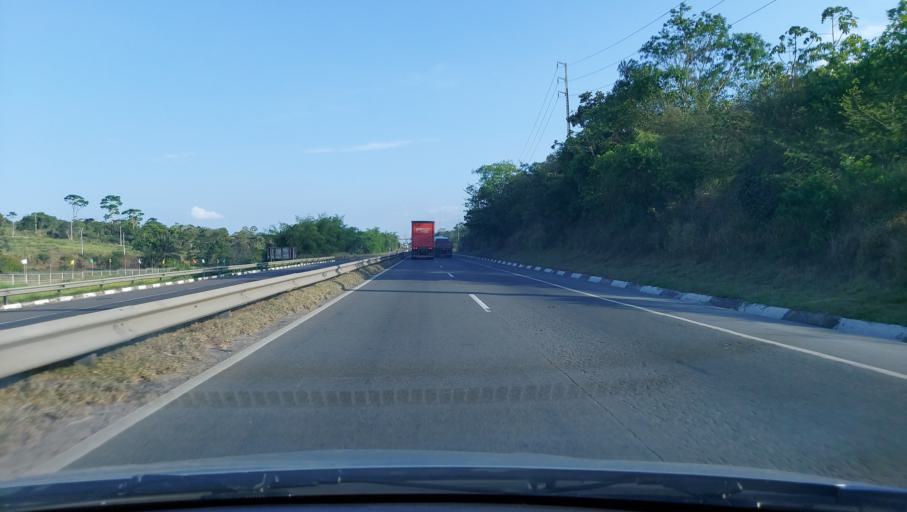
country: BR
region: Bahia
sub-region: Conceicao Do Jacuipe
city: Conceicao do Jacuipe
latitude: -12.3533
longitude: -38.8319
